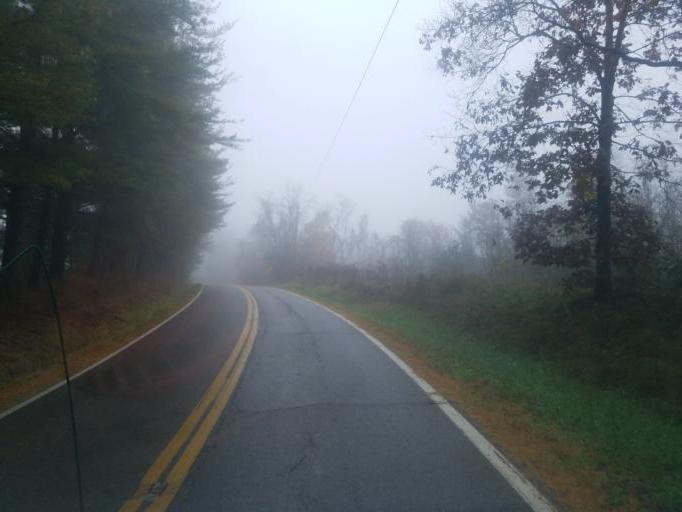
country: US
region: Ohio
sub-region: Morgan County
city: McConnelsville
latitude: 39.5393
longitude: -81.8014
